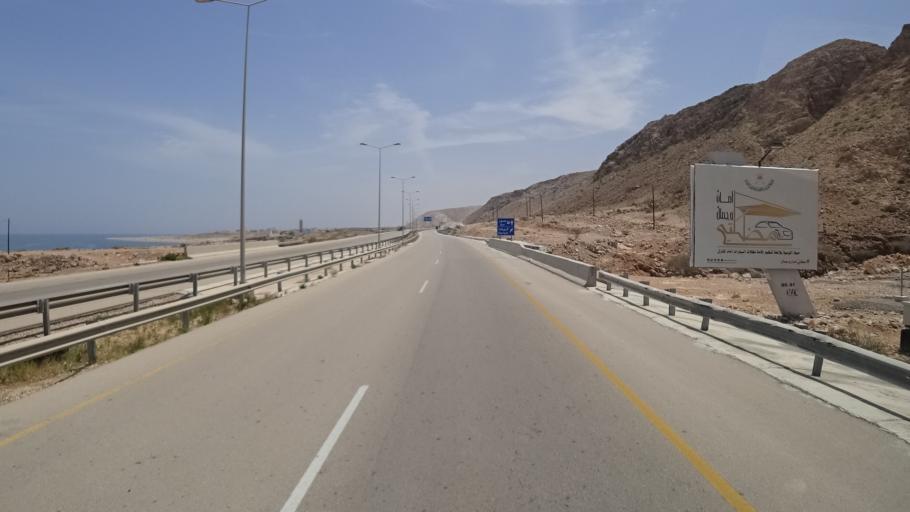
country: OM
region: Ash Sharqiyah
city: Sur
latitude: 22.7114
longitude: 59.3545
